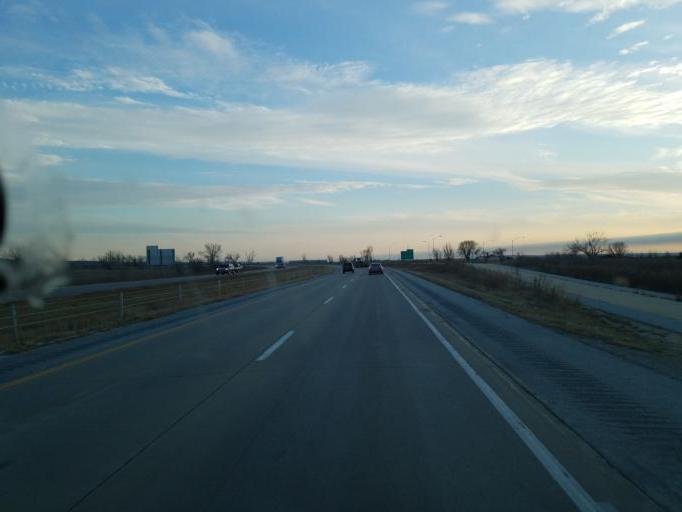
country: US
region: Iowa
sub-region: Harrison County
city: Missouri Valley
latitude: 41.5209
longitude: -95.9178
